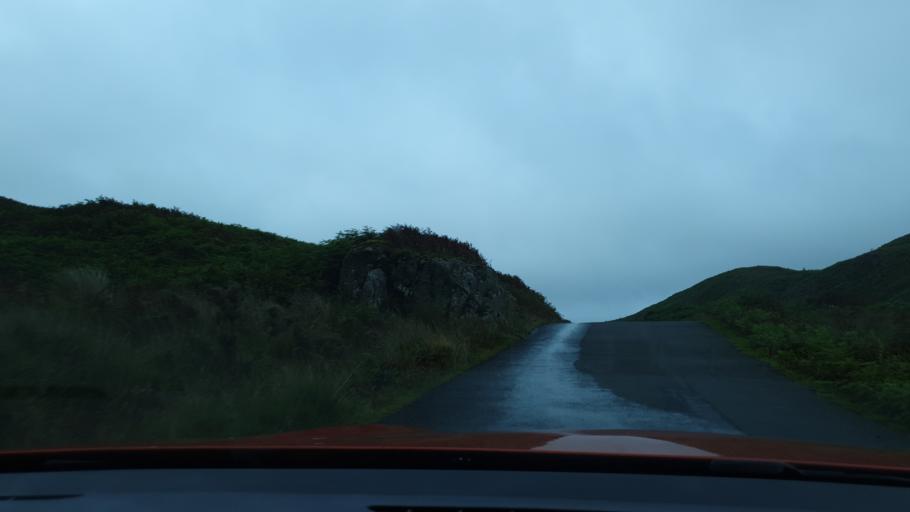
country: GB
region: England
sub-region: Cumbria
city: Millom
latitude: 54.3818
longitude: -3.2930
